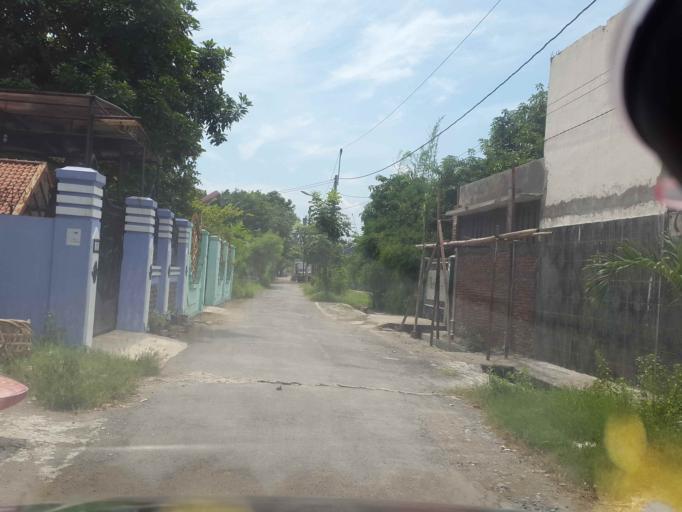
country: ID
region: Central Java
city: Tegal
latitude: -6.8651
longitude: 109.1477
